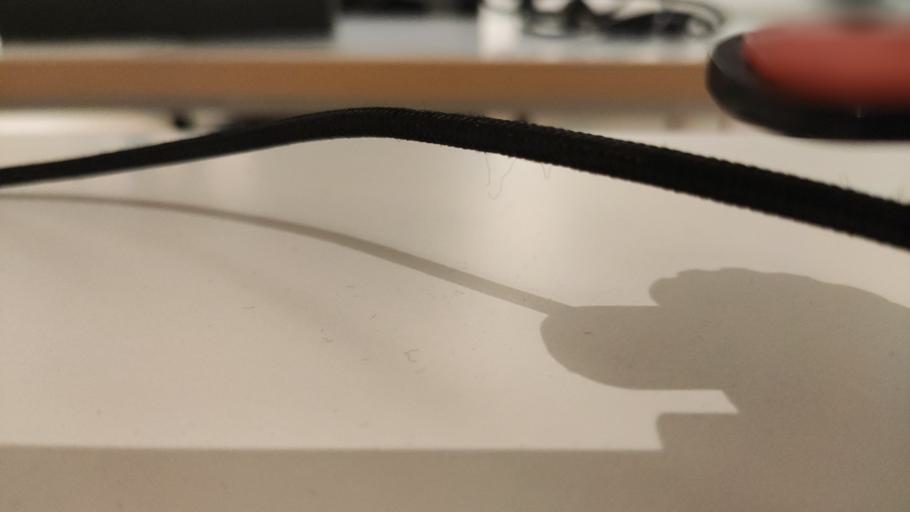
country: RU
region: Moskovskaya
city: Dorokhovo
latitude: 55.3813
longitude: 36.4009
